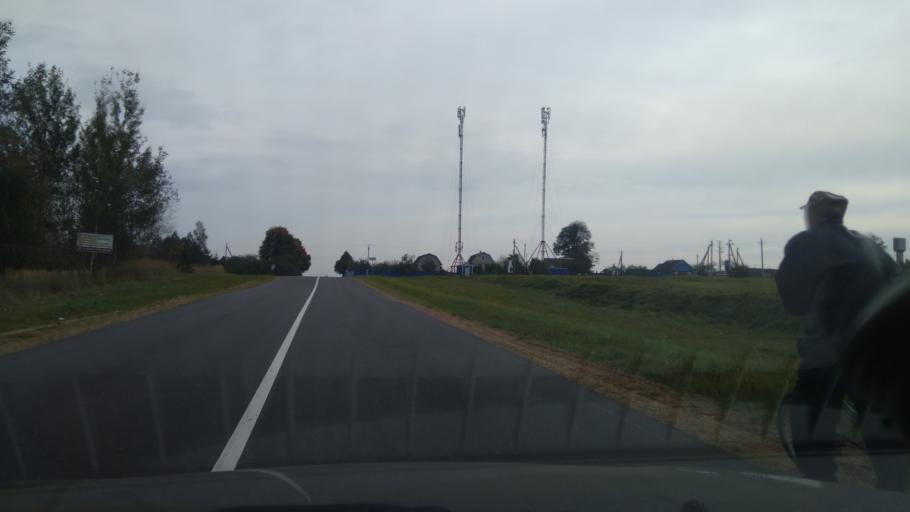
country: BY
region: Minsk
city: Rudzyensk
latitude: 53.6159
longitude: 27.7378
